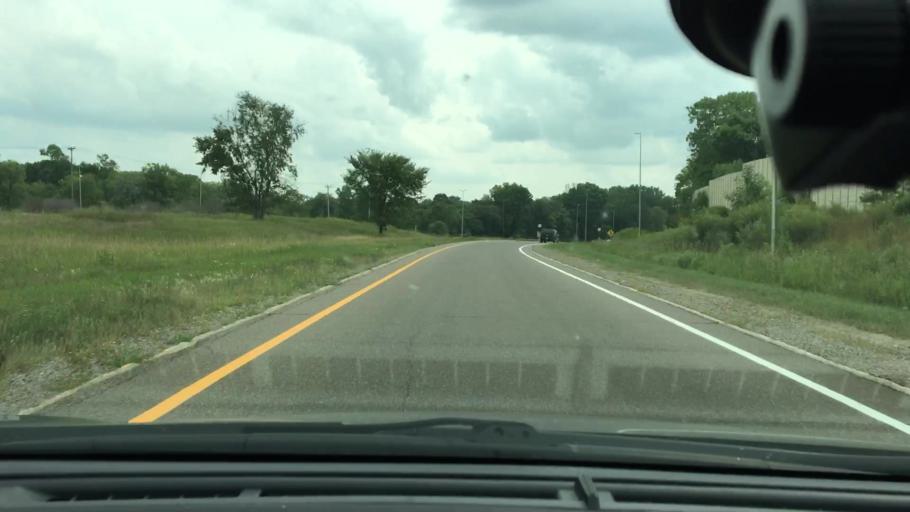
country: US
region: Minnesota
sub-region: Hennepin County
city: Osseo
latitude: 45.0818
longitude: -93.4036
